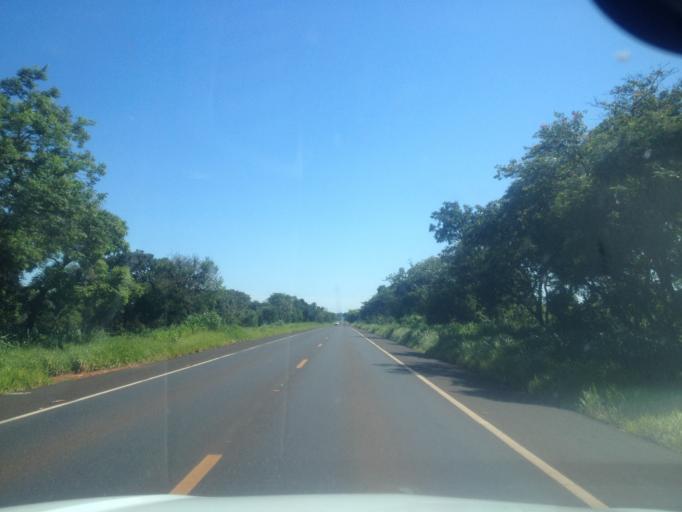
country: BR
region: Minas Gerais
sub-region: Santa Vitoria
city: Santa Vitoria
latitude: -18.9825
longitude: -50.2986
